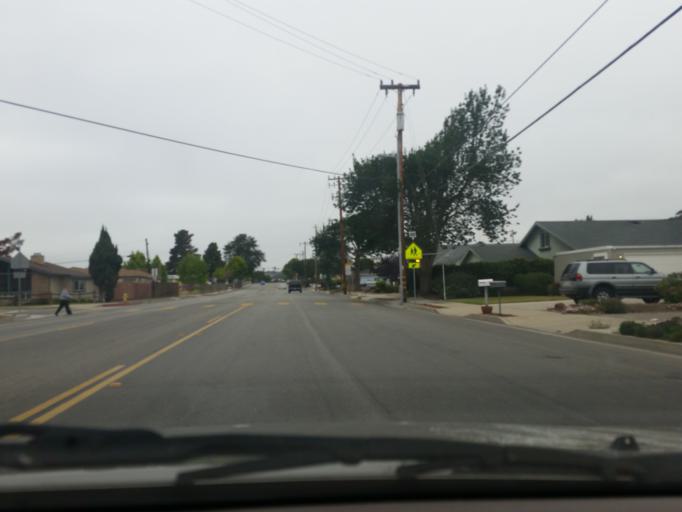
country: US
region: California
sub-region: San Luis Obispo County
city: Arroyo Grande
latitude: 35.1096
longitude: -120.5916
